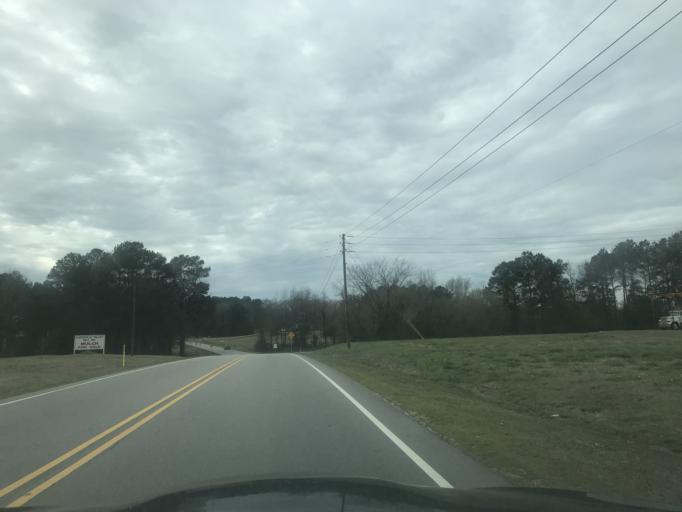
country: US
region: North Carolina
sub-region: Franklin County
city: Louisburg
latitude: 36.0886
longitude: -78.3644
